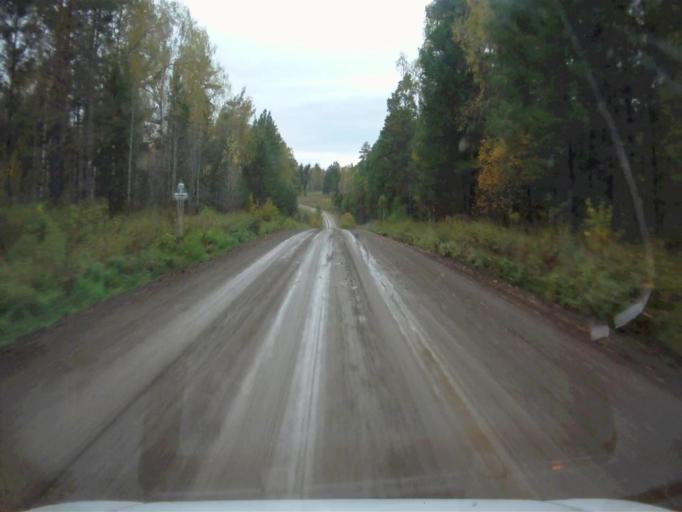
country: RU
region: Chelyabinsk
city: Nyazepetrovsk
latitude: 56.0886
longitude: 59.4158
